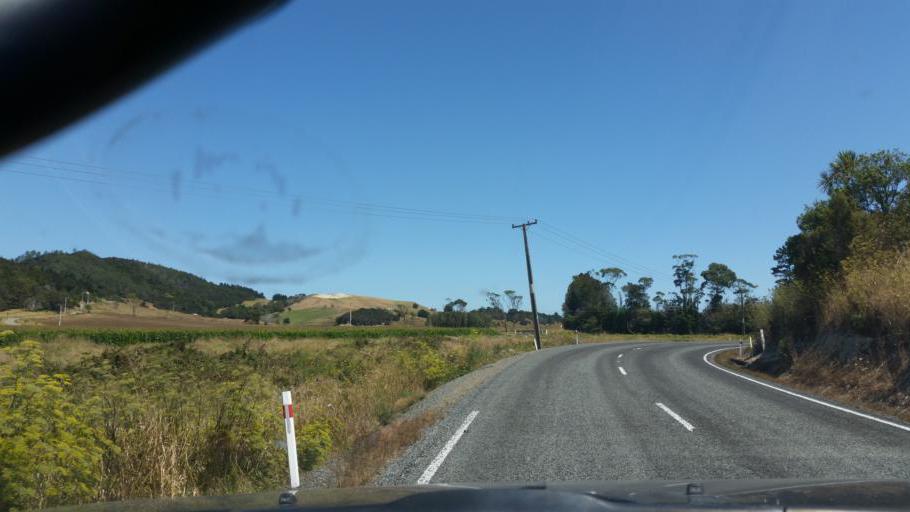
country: NZ
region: Northland
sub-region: Kaipara District
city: Dargaville
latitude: -36.0069
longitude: 173.9602
